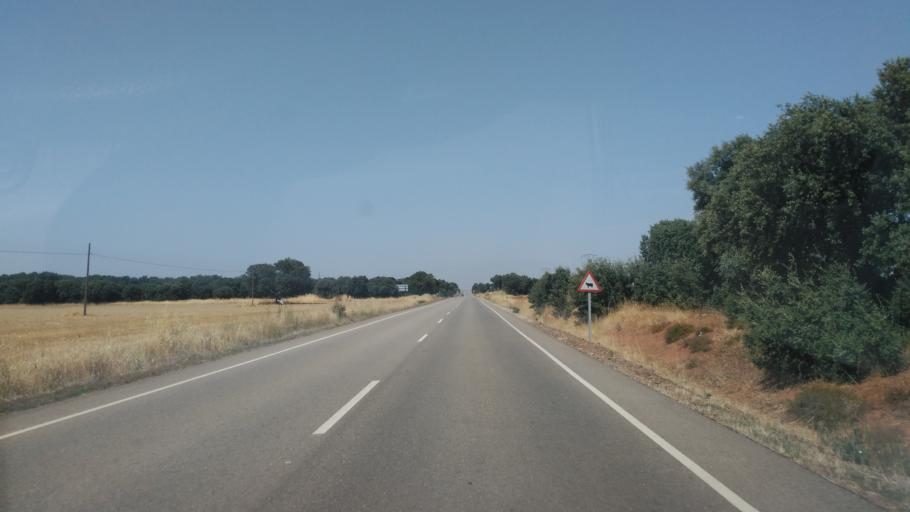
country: ES
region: Castille and Leon
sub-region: Provincia de Salamanca
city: Cabrillas
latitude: 40.7588
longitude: -6.1975
